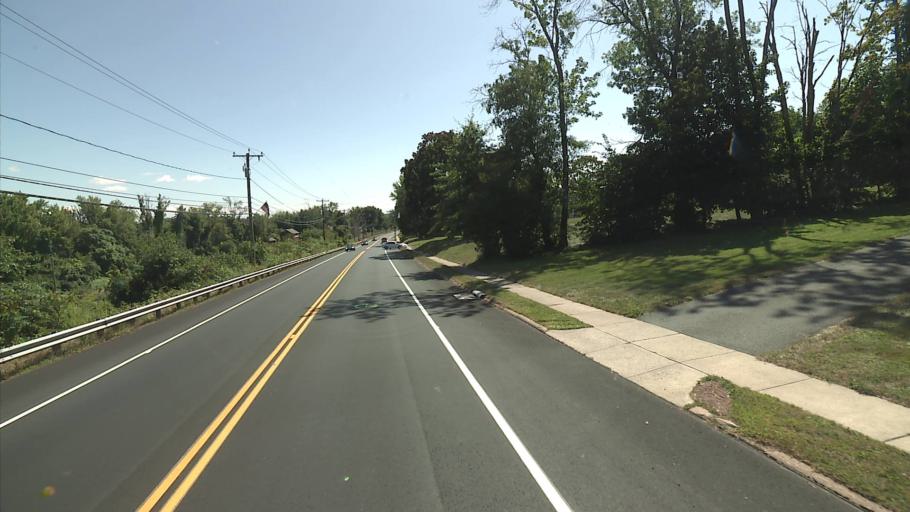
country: US
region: Connecticut
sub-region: Hartford County
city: Windsor Locks
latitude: 41.9212
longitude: -72.6260
